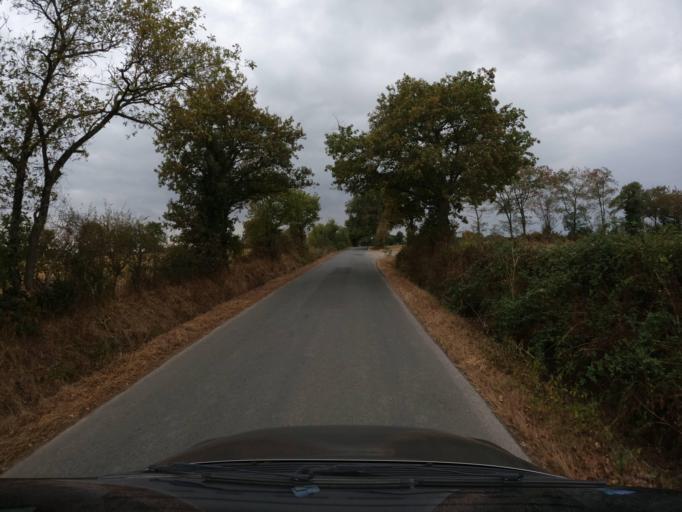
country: FR
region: Pays de la Loire
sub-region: Departement de la Vendee
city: La Boissiere-de-Montaigu
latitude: 46.9778
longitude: -1.1771
